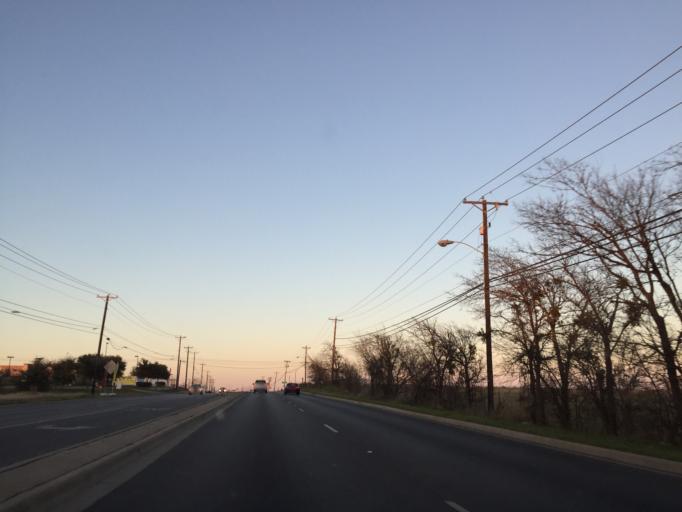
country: US
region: Texas
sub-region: Travis County
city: Pflugerville
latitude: 30.4471
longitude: -97.6071
